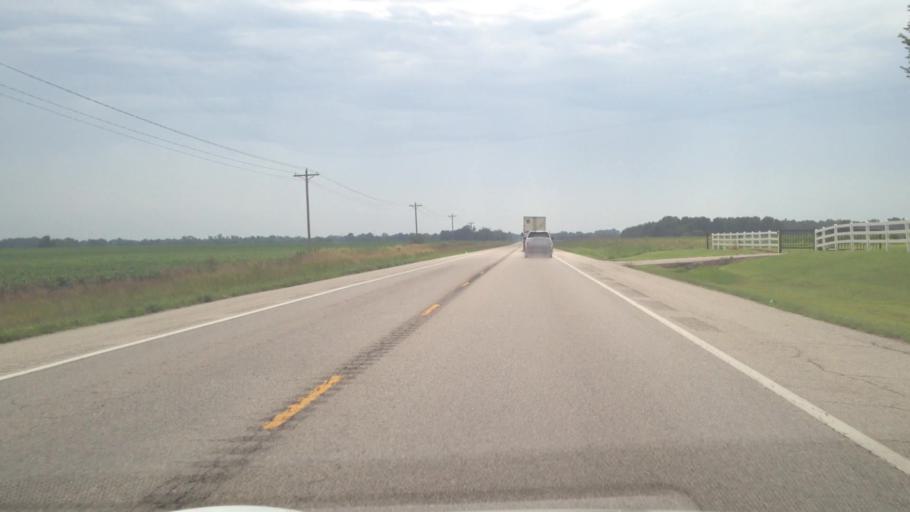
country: US
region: Kansas
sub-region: Crawford County
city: Pittsburg
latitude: 37.2726
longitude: -94.7053
